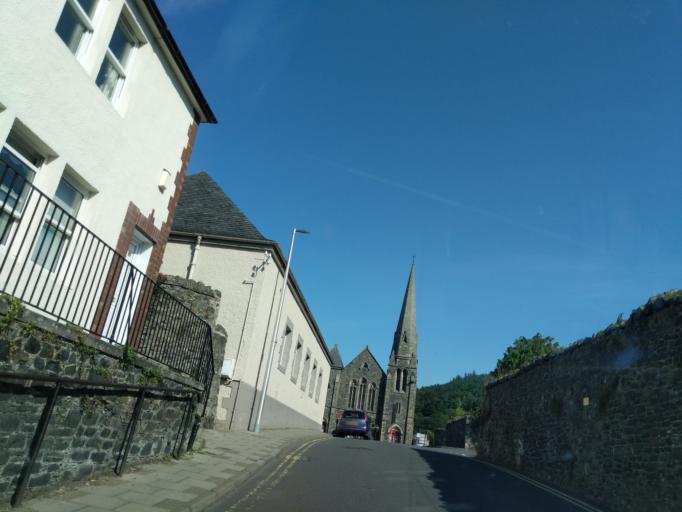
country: GB
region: Scotland
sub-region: The Scottish Borders
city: Peebles
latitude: 55.6514
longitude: -3.1874
